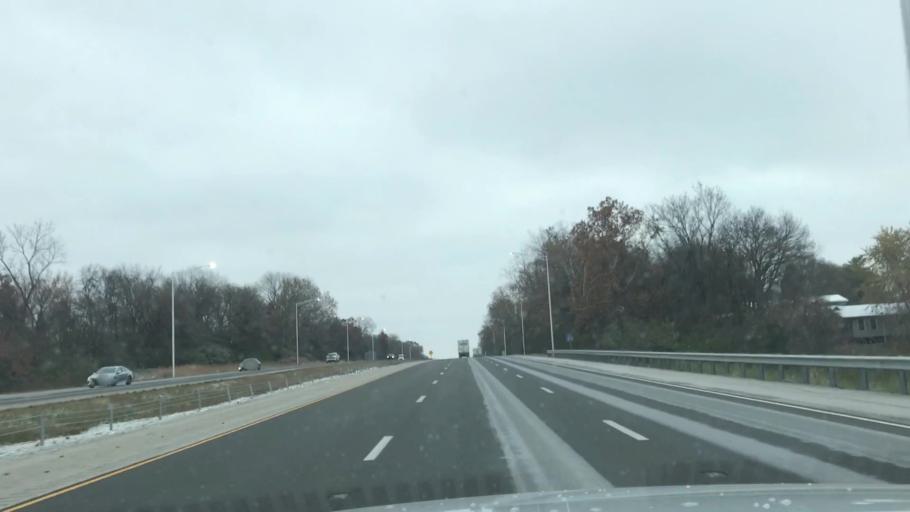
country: US
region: Illinois
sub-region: Madison County
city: Glen Carbon
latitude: 38.7564
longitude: -90.0006
